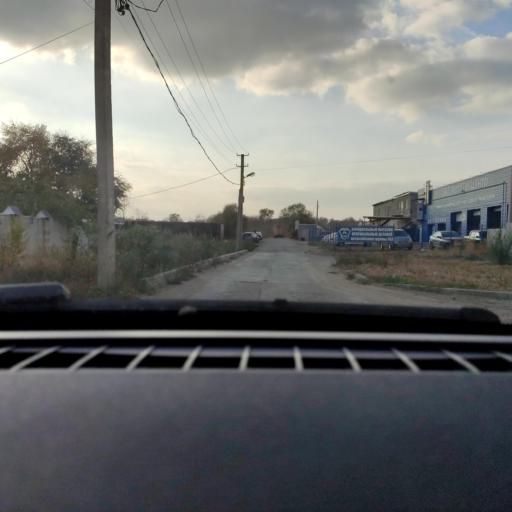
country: RU
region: Voronezj
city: Voronezh
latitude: 51.6680
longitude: 39.2803
